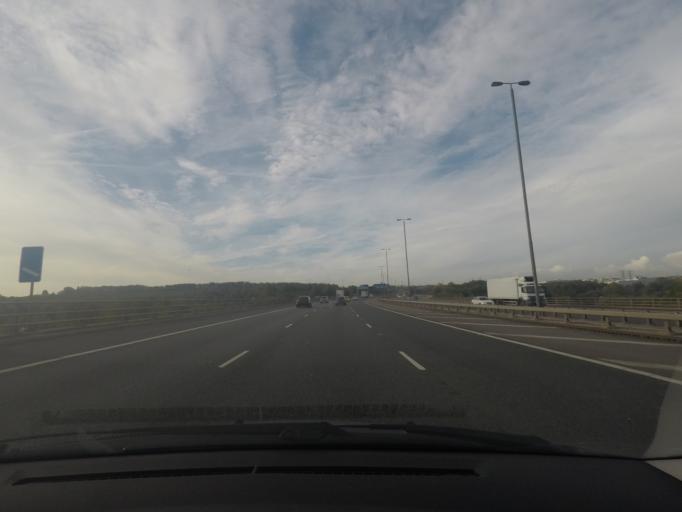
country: GB
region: England
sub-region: City and Borough of Leeds
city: Lofthouse
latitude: 53.7658
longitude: -1.4824
